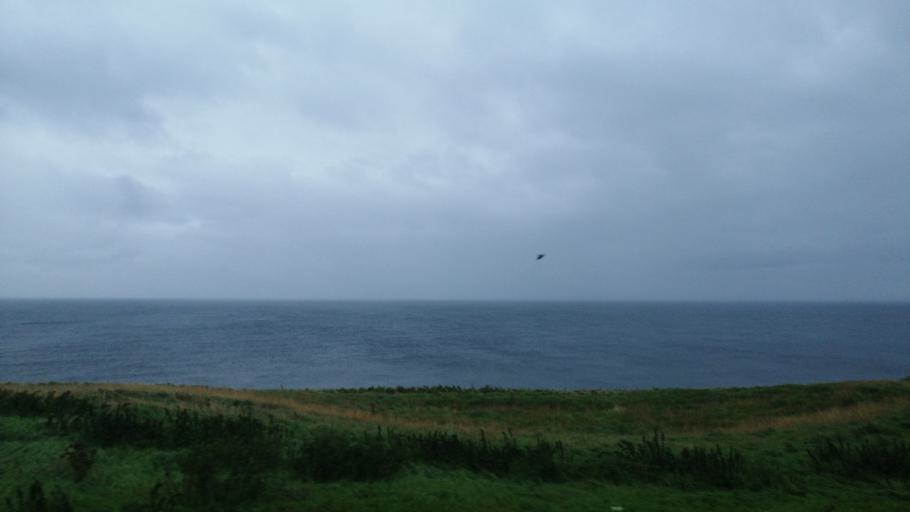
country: GB
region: Scotland
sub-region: Highland
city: Brora
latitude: 58.0044
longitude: -3.8650
